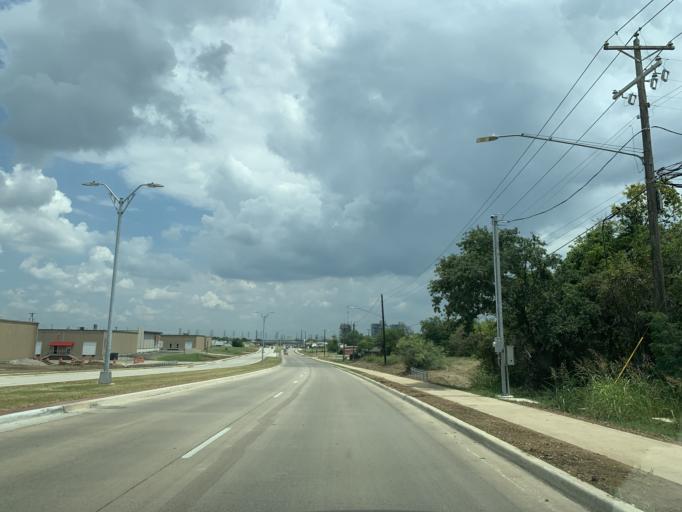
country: US
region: Texas
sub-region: Tarrant County
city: Forest Hill
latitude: 32.7295
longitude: -97.2316
